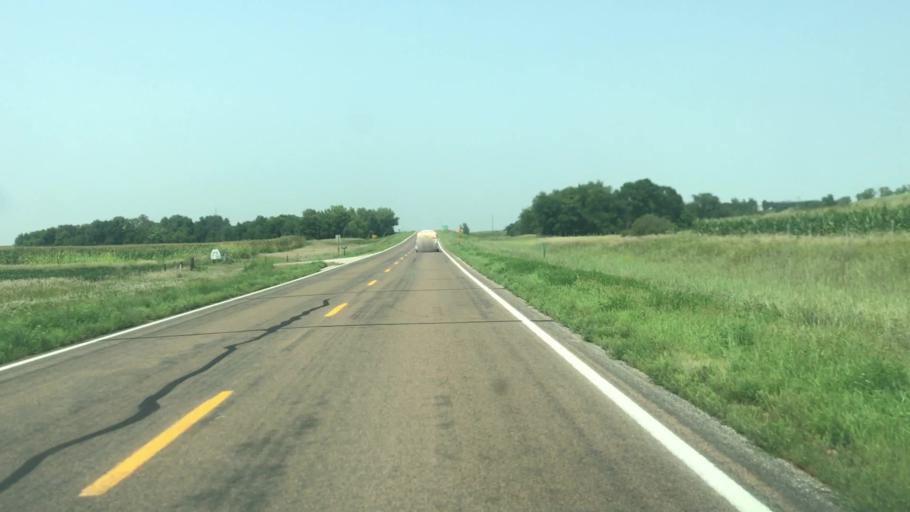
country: US
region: Nebraska
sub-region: Sherman County
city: Loup City
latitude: 41.2568
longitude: -98.9389
